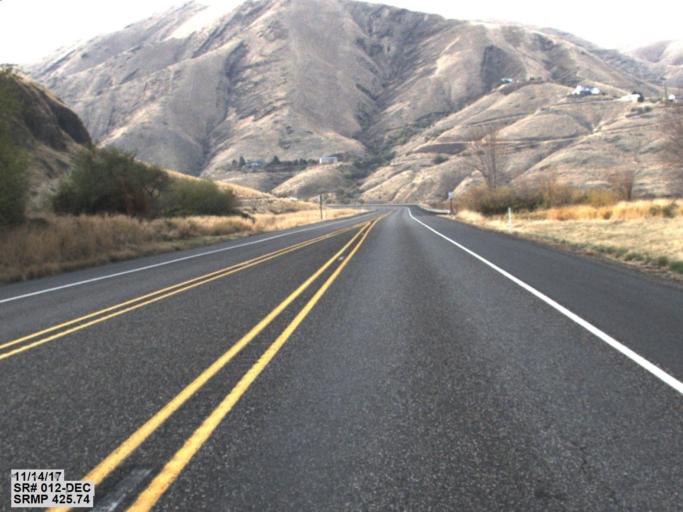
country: US
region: Washington
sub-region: Asotin County
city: Clarkston Heights-Vineland
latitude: 46.4140
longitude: -117.2001
